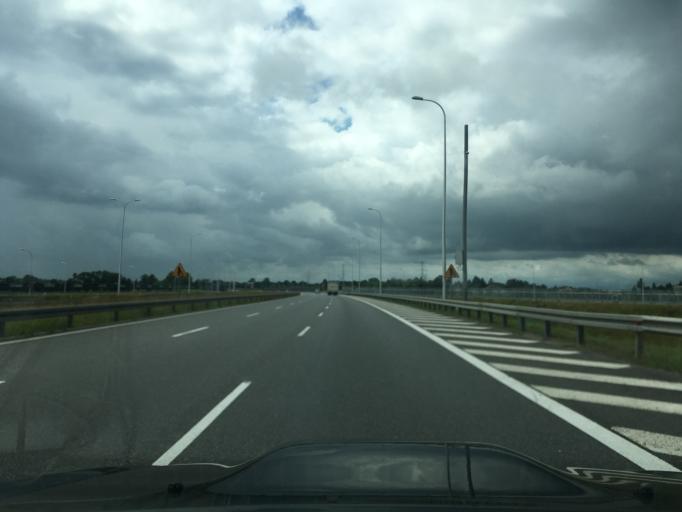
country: PL
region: Lublin Voivodeship
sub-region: Powiat lubelski
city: Lublin
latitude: 51.3025
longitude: 22.5862
